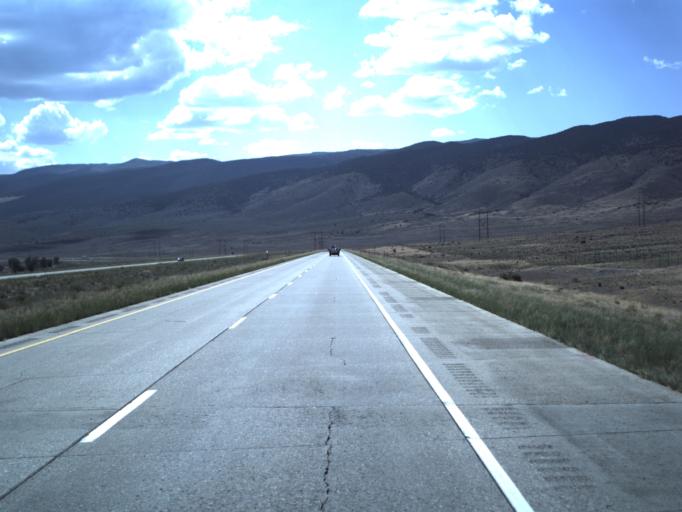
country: US
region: Utah
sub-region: Sevier County
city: Monroe
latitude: 38.6590
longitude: -112.1892
